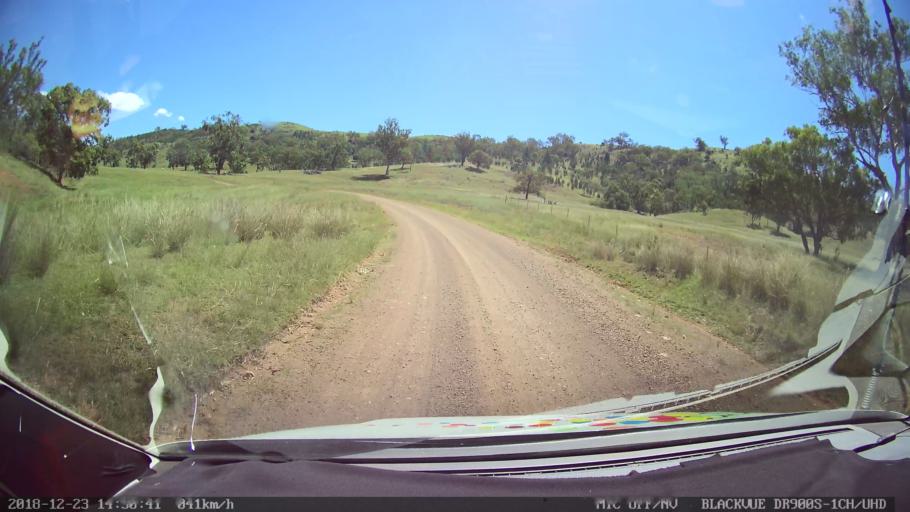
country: AU
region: New South Wales
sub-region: Tamworth Municipality
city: Manilla
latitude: -30.6723
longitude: 150.8561
